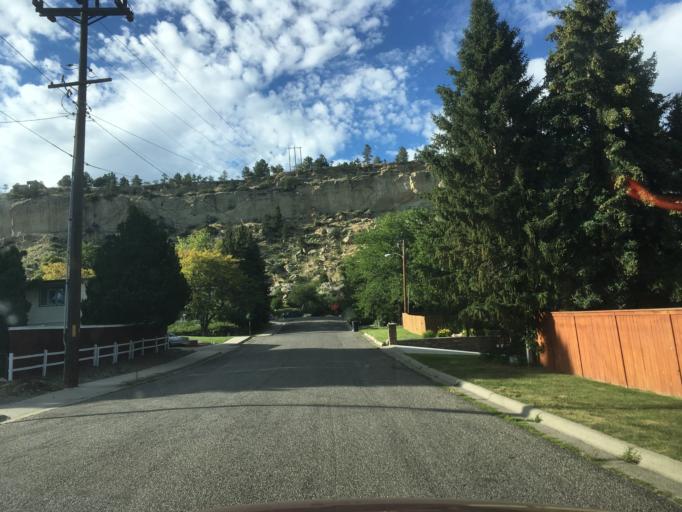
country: US
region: Montana
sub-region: Yellowstone County
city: Billings
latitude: 45.7998
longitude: -108.5761
